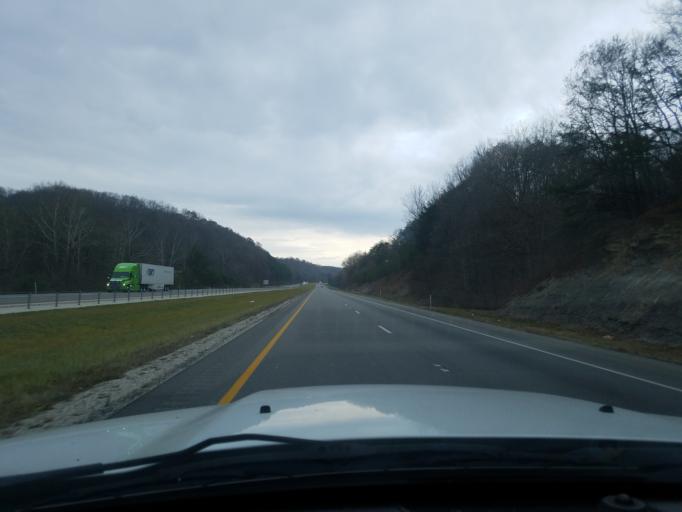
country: US
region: Kentucky
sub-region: Boyd County
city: Meads
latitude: 38.3648
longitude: -82.7909
